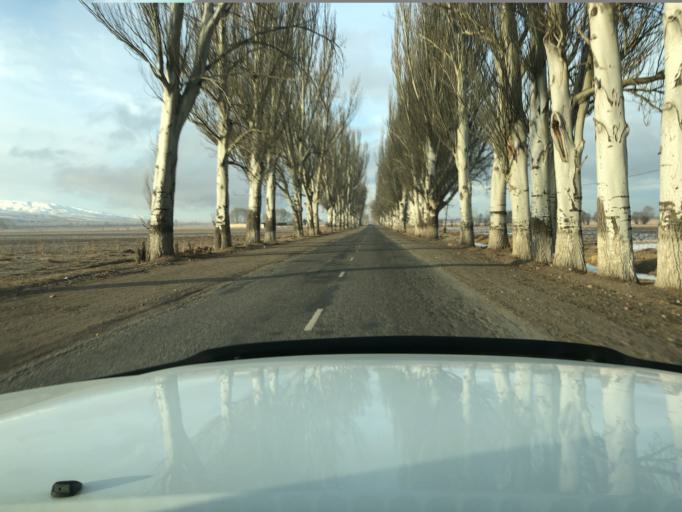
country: KG
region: Ysyk-Koel
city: Karakol
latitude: 42.4775
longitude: 78.3321
